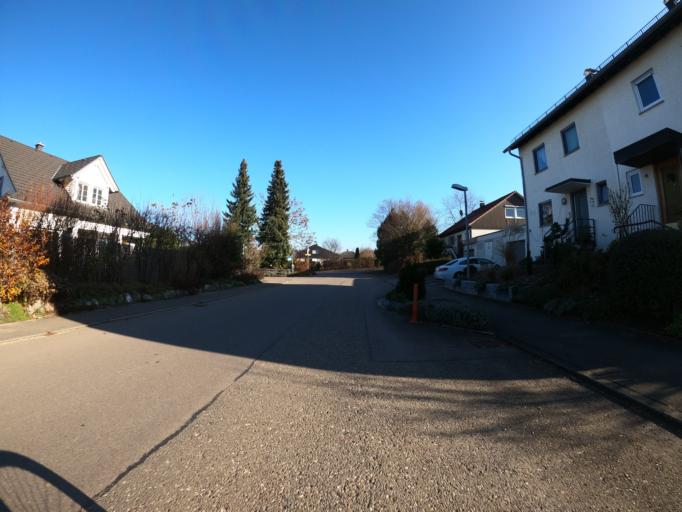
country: DE
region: Baden-Wuerttemberg
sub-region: Regierungsbezirk Stuttgart
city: Gammelshausen
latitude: 48.6438
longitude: 9.6525
